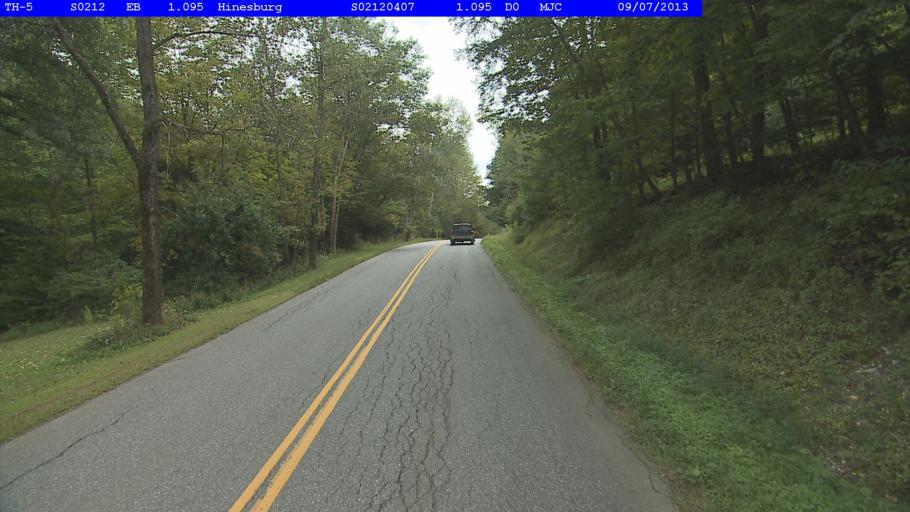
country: US
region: Vermont
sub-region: Chittenden County
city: Hinesburg
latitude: 44.2929
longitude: -73.0488
